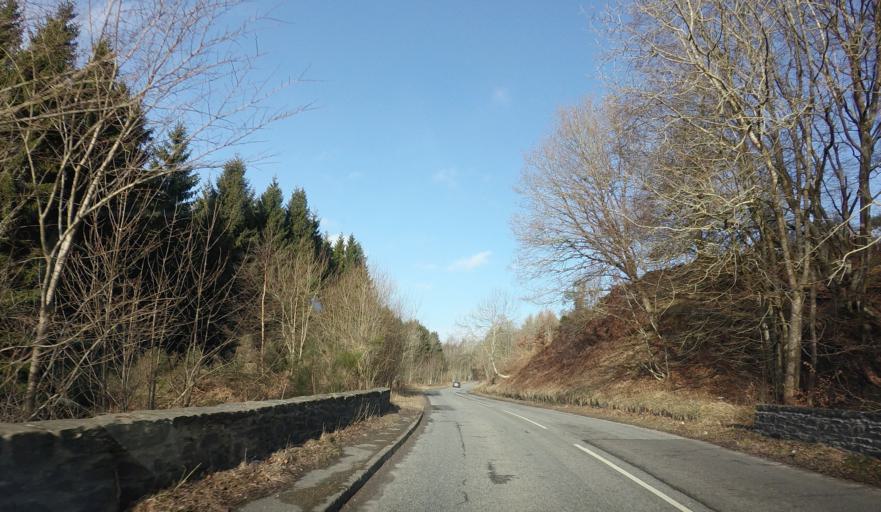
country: GB
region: Scotland
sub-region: Perth and Kinross
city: Pitlochry
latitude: 56.6012
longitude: -3.6251
